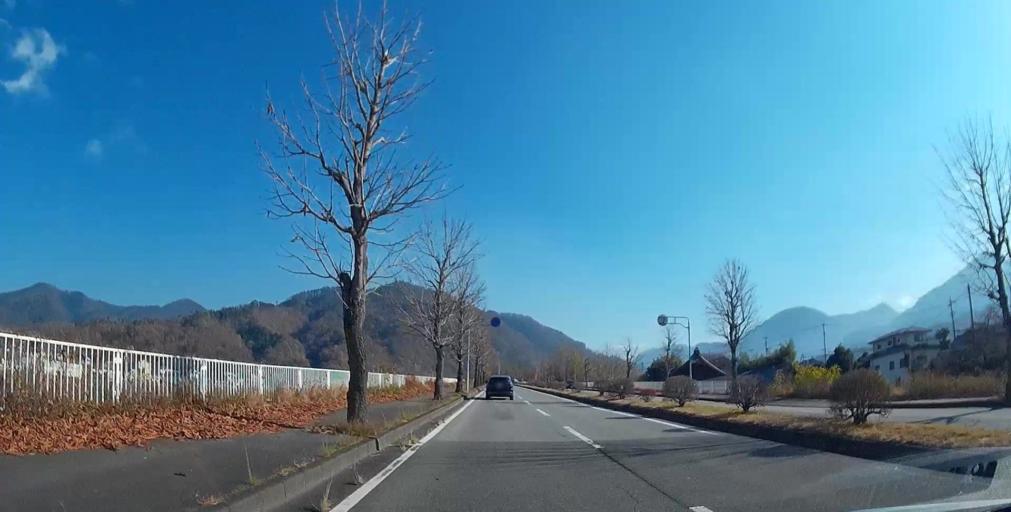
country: JP
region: Yamanashi
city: Isawa
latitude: 35.6210
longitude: 138.6914
